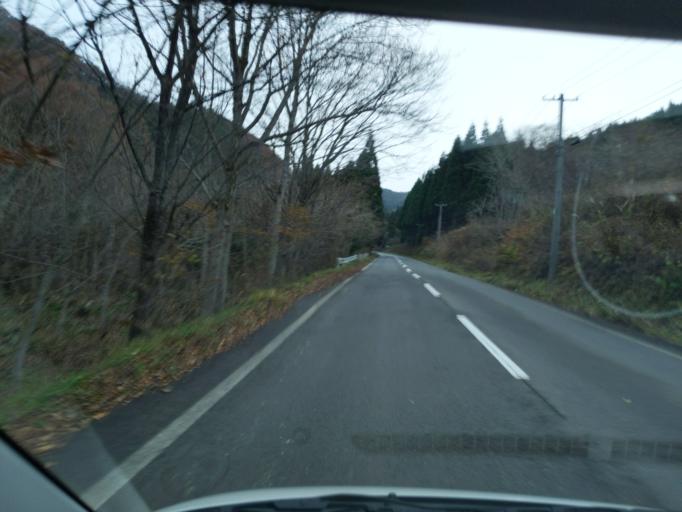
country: JP
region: Iwate
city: Tono
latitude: 39.1840
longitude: 141.3575
